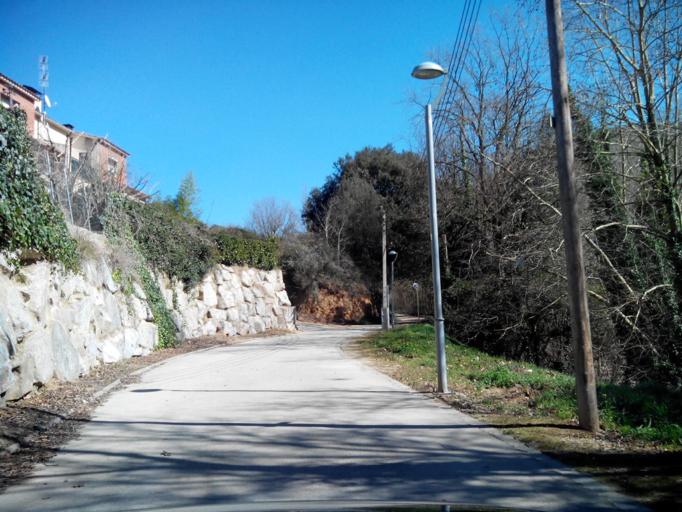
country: ES
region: Catalonia
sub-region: Provincia de Barcelona
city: Dosrius
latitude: 41.6016
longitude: 2.4493
